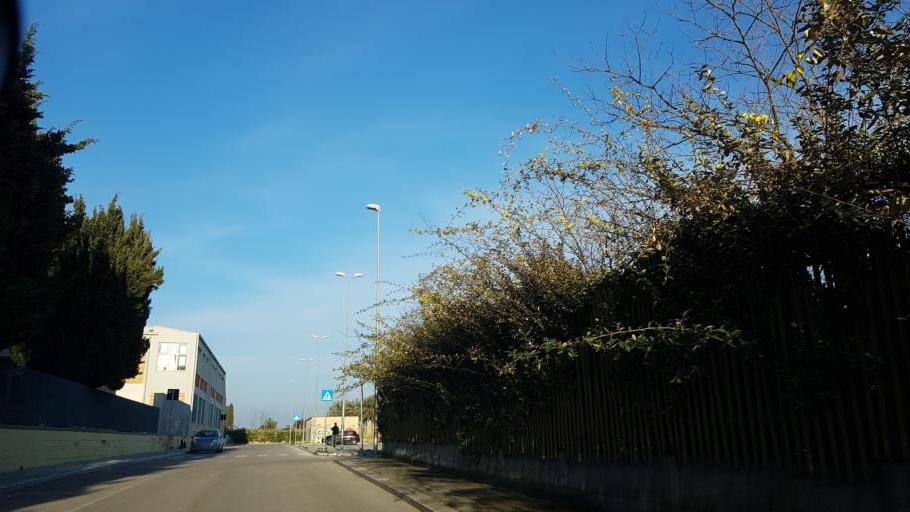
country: IT
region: Apulia
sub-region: Provincia di Brindisi
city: Brindisi
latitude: 40.6257
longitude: 17.9357
